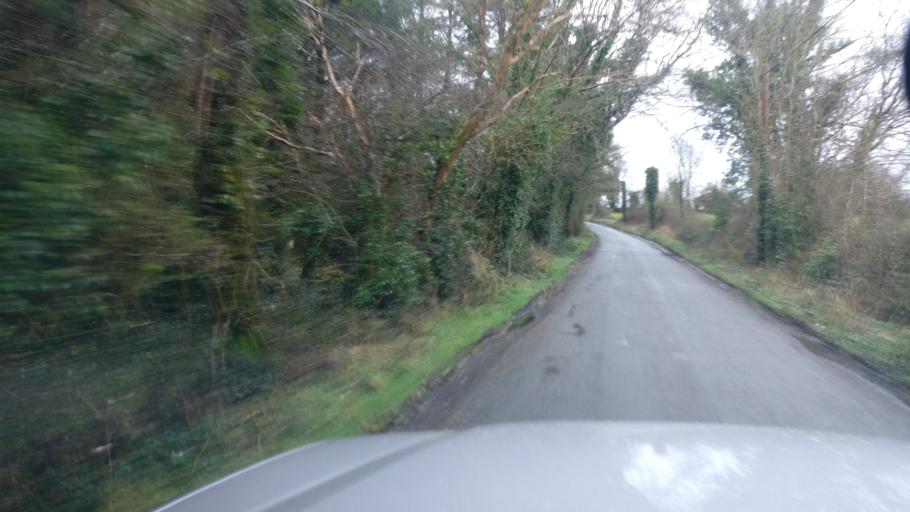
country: IE
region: Connaught
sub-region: County Galway
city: Ballinasloe
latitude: 53.2603
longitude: -8.3558
